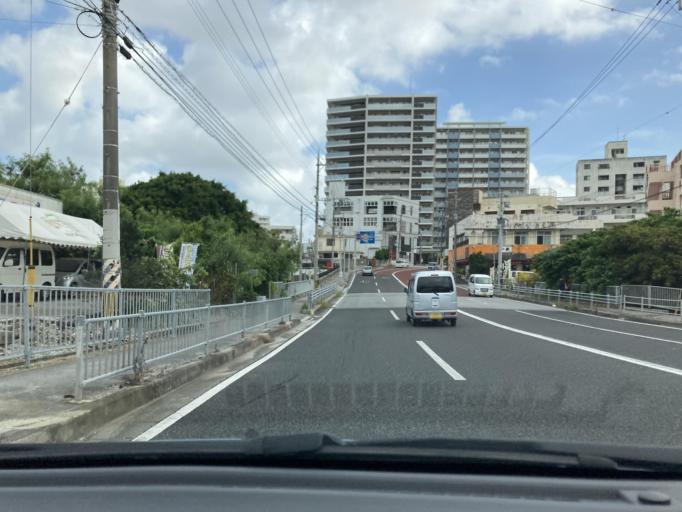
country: JP
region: Okinawa
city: Ginowan
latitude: 26.2582
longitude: 127.7415
